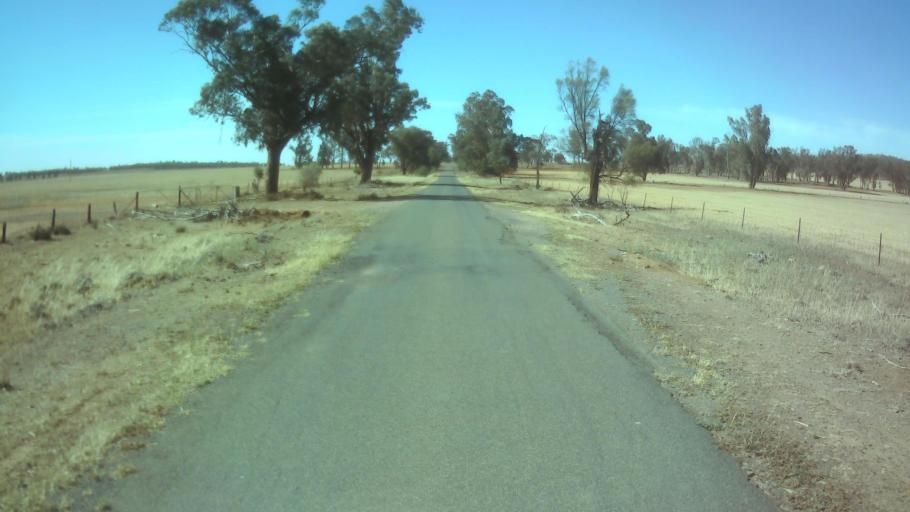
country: AU
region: New South Wales
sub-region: Forbes
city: Forbes
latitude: -33.7353
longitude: 147.7420
